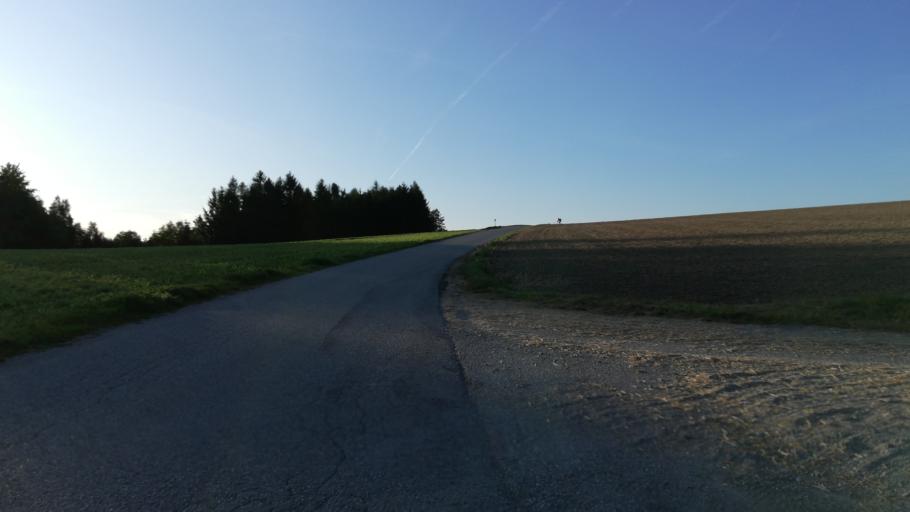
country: AT
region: Upper Austria
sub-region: Wels-Land
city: Offenhausen
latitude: 48.1622
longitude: 13.8605
